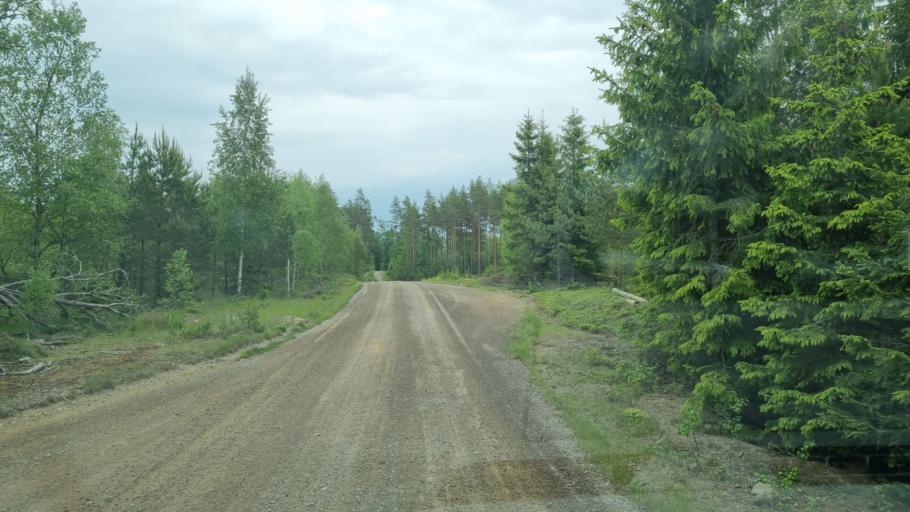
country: SE
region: OEstergoetland
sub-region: Atvidabergs Kommun
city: Atvidaberg
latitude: 58.2582
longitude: 16.0576
